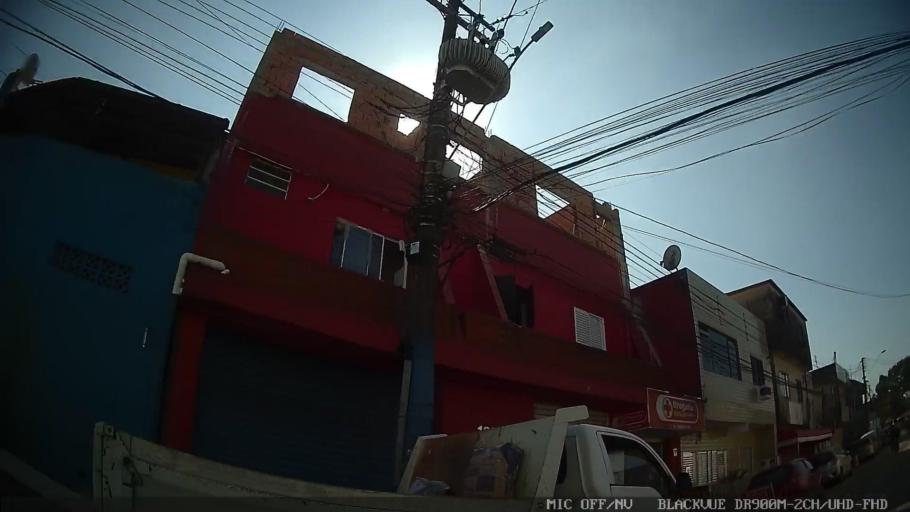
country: BR
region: Sao Paulo
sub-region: Santos
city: Santos
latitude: -23.9967
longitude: -46.3034
